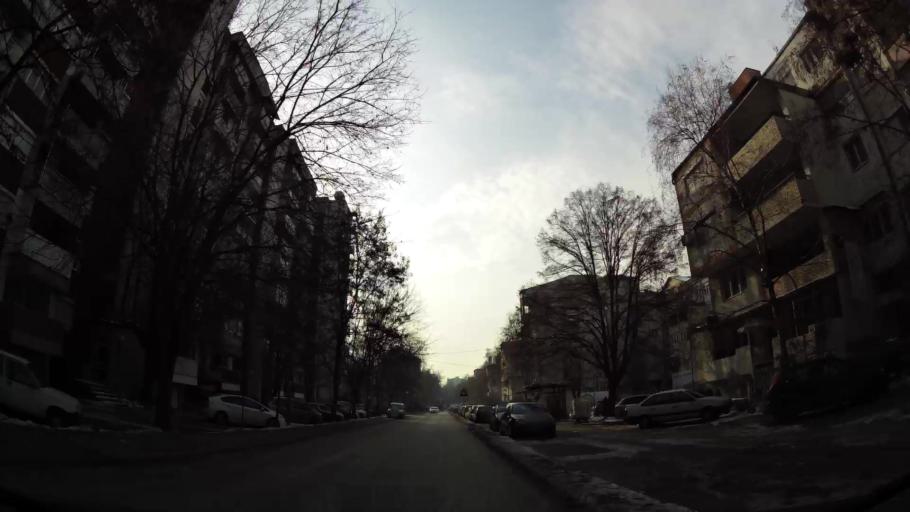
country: MK
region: Cair
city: Cair
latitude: 42.0206
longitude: 21.4322
